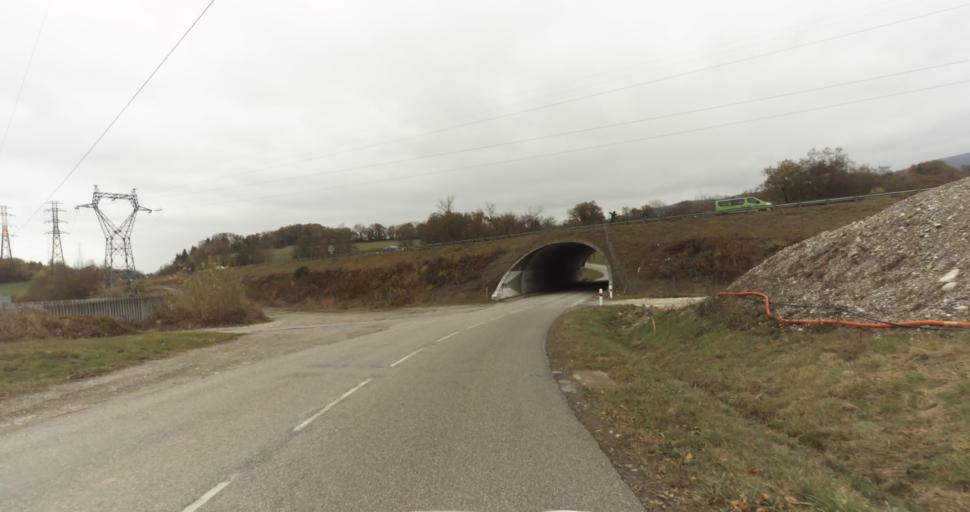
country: FR
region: Rhone-Alpes
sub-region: Departement de la Haute-Savoie
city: Chavanod
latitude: 45.8639
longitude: 6.0572
